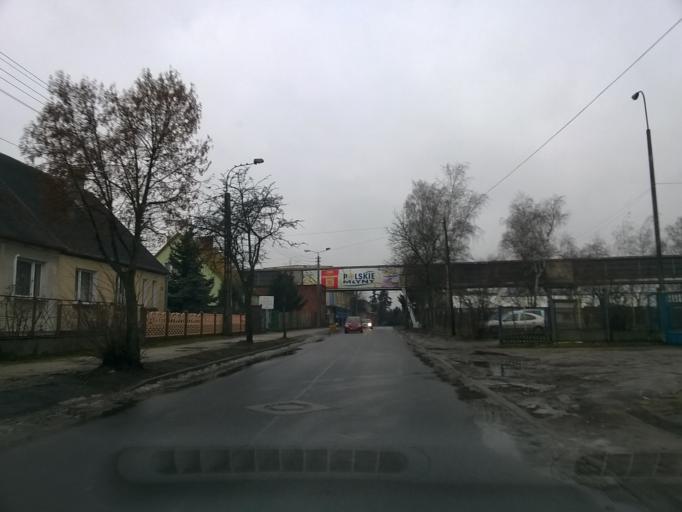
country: PL
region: Kujawsko-Pomorskie
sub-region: Powiat nakielski
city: Naklo nad Notecia
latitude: 53.1343
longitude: 17.5827
